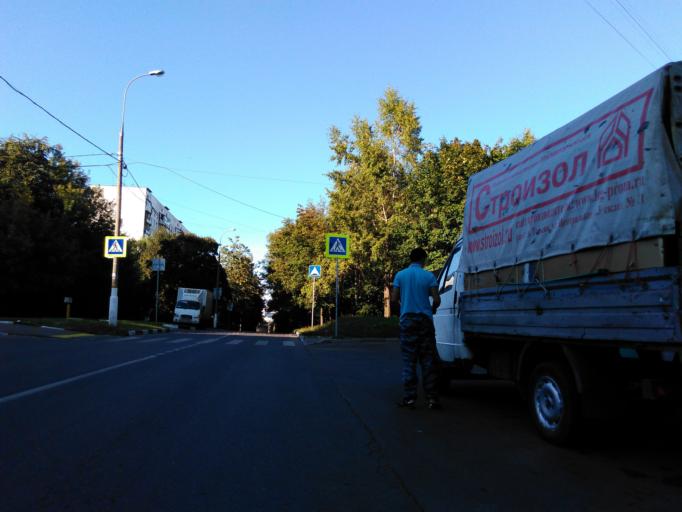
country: RU
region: Moscow
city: Tyoply Stan
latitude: 55.6432
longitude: 37.5127
